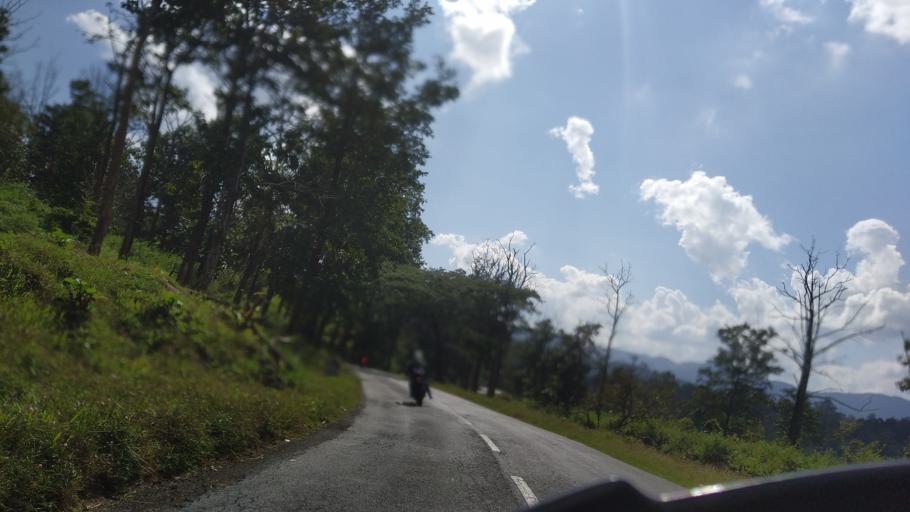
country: IN
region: Kerala
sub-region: Wayanad
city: Panamaram
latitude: 11.9183
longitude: 76.0649
